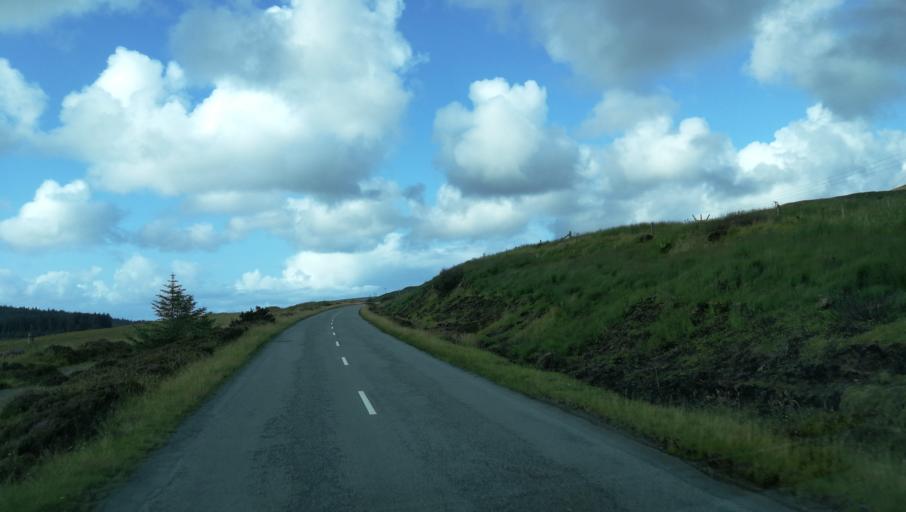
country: GB
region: Scotland
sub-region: Highland
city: Isle of Skye
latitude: 57.4509
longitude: -6.5437
